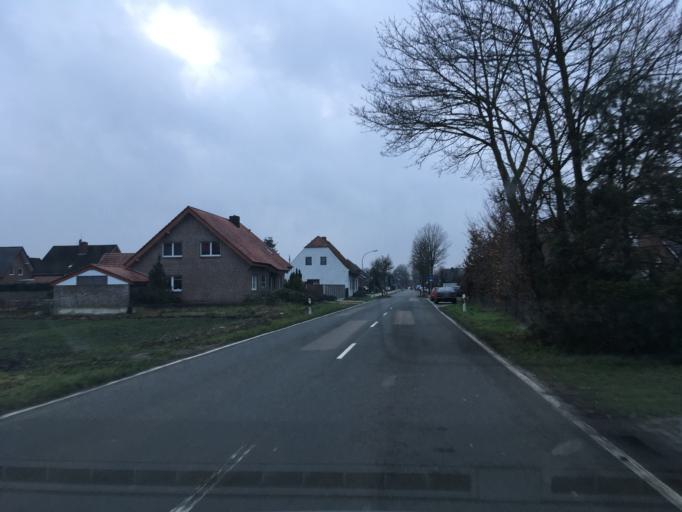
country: DE
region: North Rhine-Westphalia
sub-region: Regierungsbezirk Munster
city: Gronau
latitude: 52.1794
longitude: 7.0667
